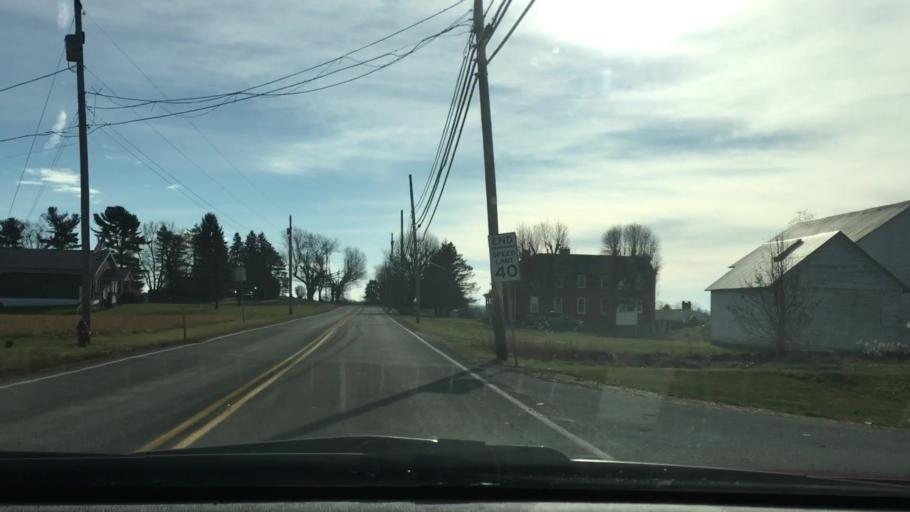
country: US
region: Pennsylvania
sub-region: Westmoreland County
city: West Newton
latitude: 40.2018
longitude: -79.7468
